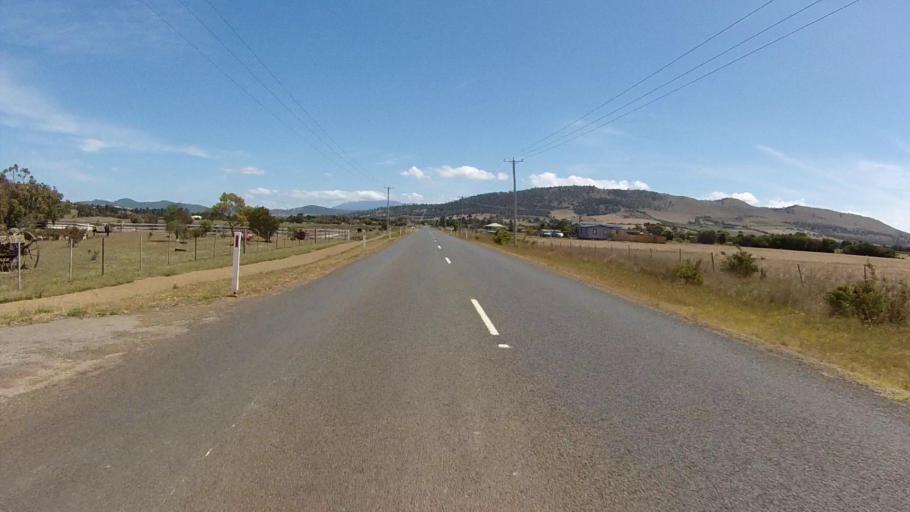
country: AU
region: Tasmania
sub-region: Sorell
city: Sorell
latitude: -42.7763
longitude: 147.5311
